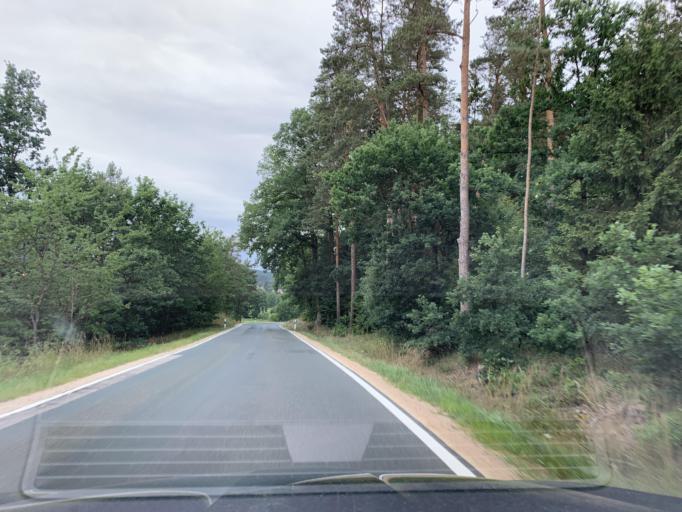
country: DE
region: Bavaria
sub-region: Upper Palatinate
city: Pettendorf
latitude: 49.3639
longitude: 12.3599
